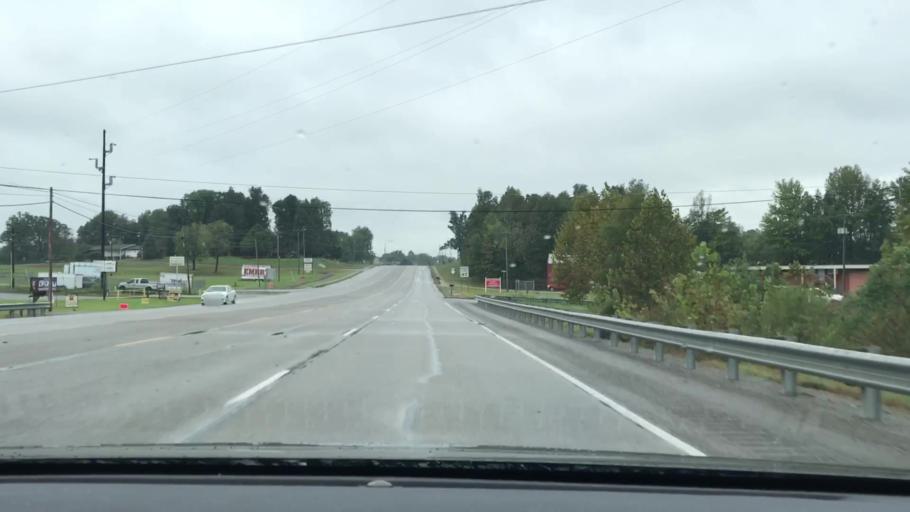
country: US
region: Kentucky
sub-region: Hopkins County
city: Madisonville
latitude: 37.3312
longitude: -87.4300
